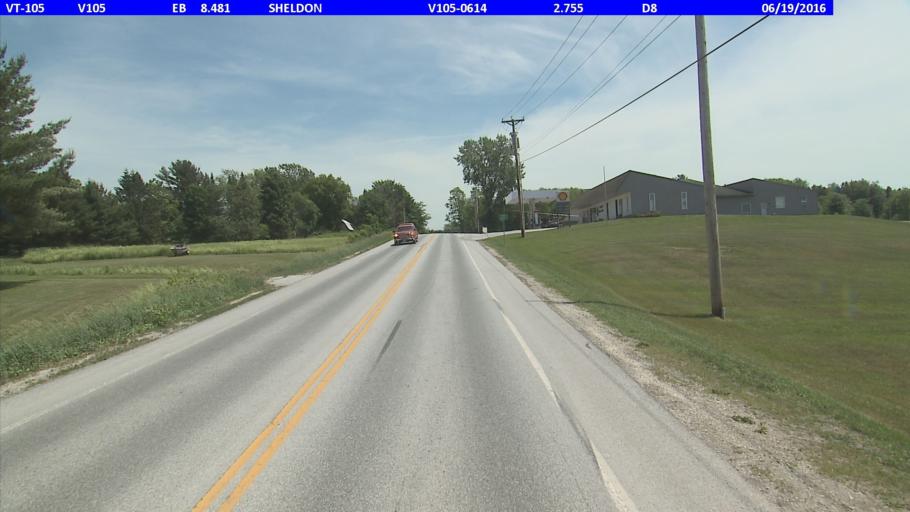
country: US
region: Vermont
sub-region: Franklin County
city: Saint Albans
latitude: 44.9037
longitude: -72.9772
